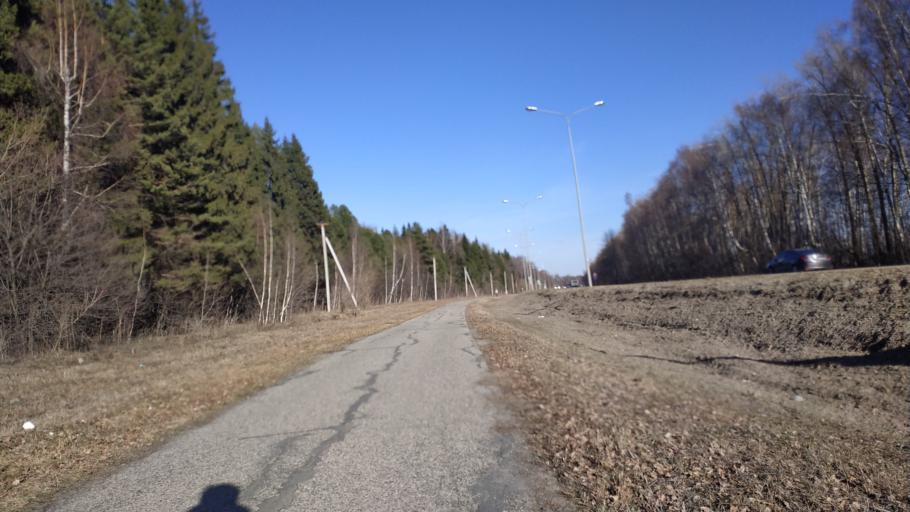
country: RU
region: Chuvashia
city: Ishley
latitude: 56.1350
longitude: 47.0953
